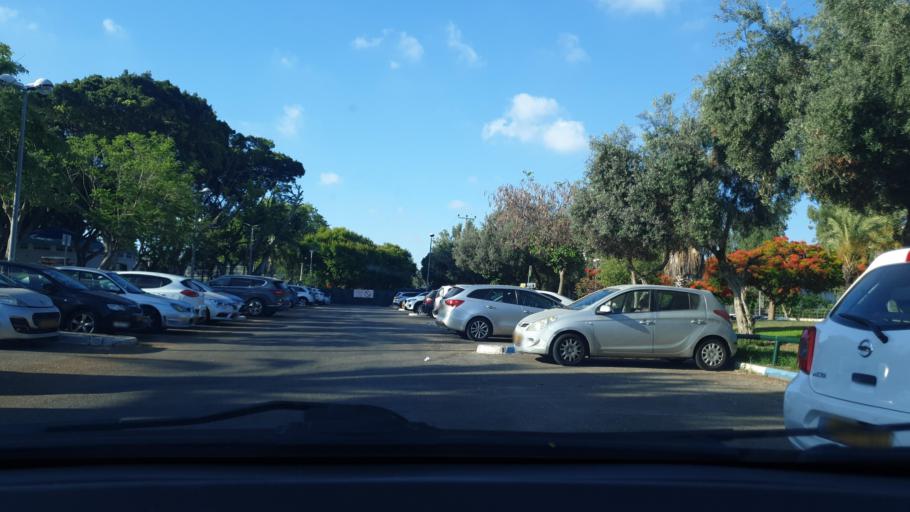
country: IL
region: Tel Aviv
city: Giv`atayim
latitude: 32.0571
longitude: 34.8065
